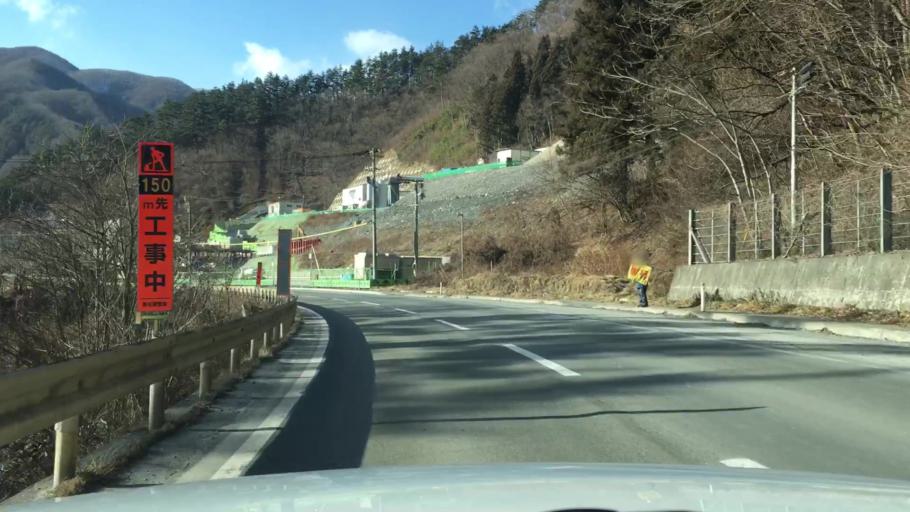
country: JP
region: Iwate
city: Miyako
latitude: 39.5964
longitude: 141.6579
